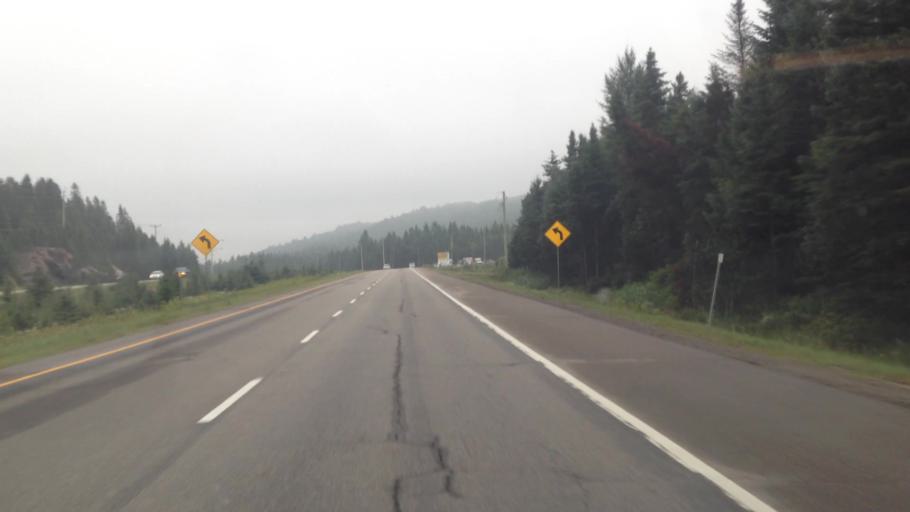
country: CA
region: Quebec
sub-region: Laurentides
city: Sainte-Agathe-des-Monts
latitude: 46.1003
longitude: -74.3769
